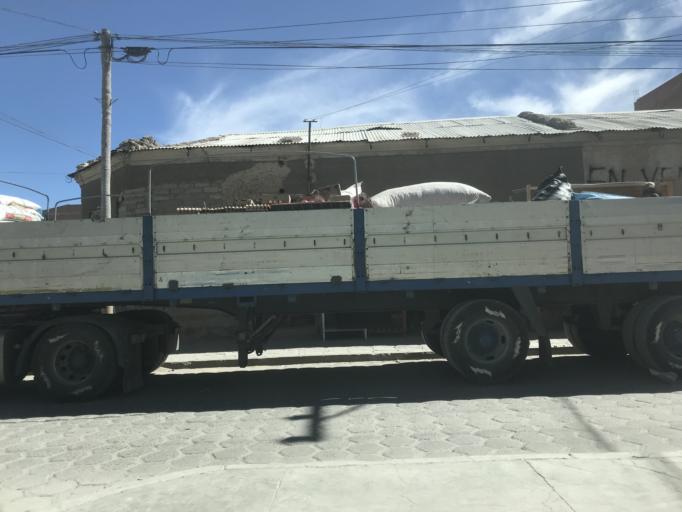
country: BO
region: Potosi
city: Uyuni
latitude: -20.4636
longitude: -66.8264
